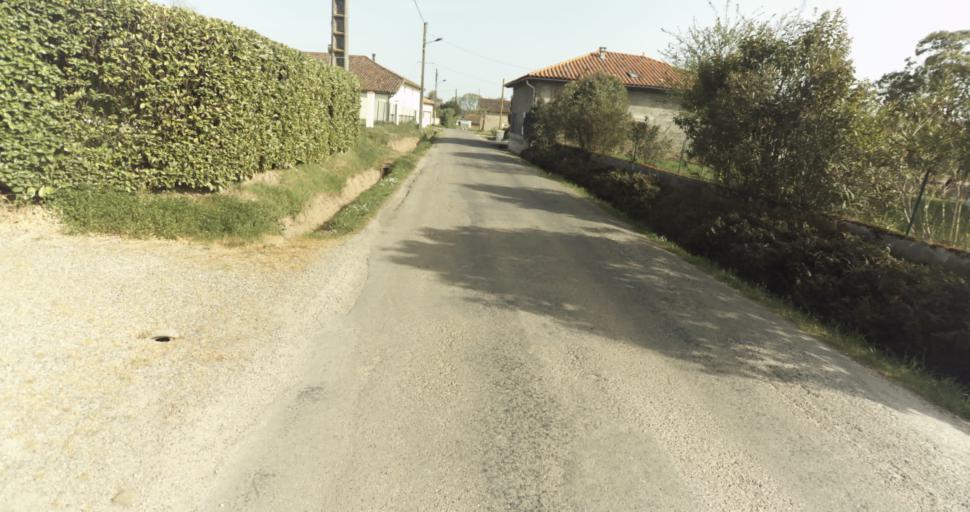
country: FR
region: Midi-Pyrenees
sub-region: Departement du Tarn-et-Garonne
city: Moissac
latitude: 44.1217
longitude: 1.1501
